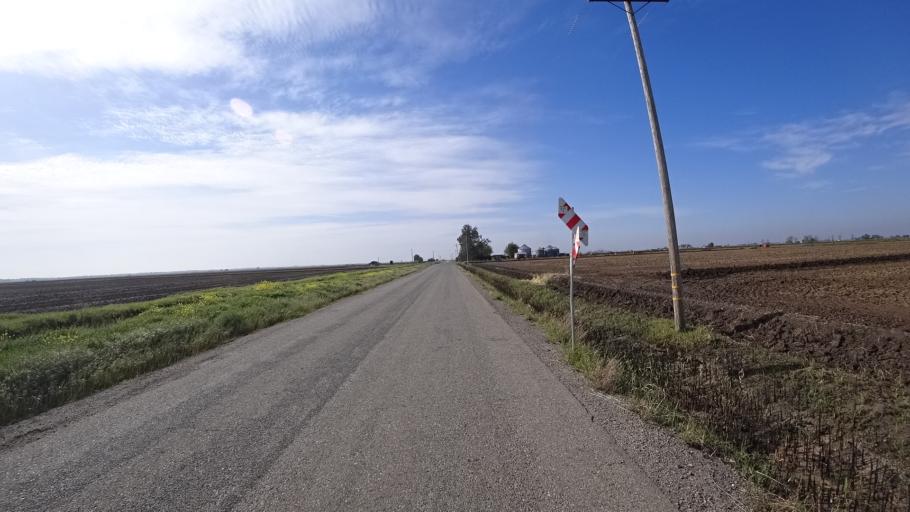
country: US
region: California
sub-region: Glenn County
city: Willows
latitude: 39.5744
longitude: -122.0464
